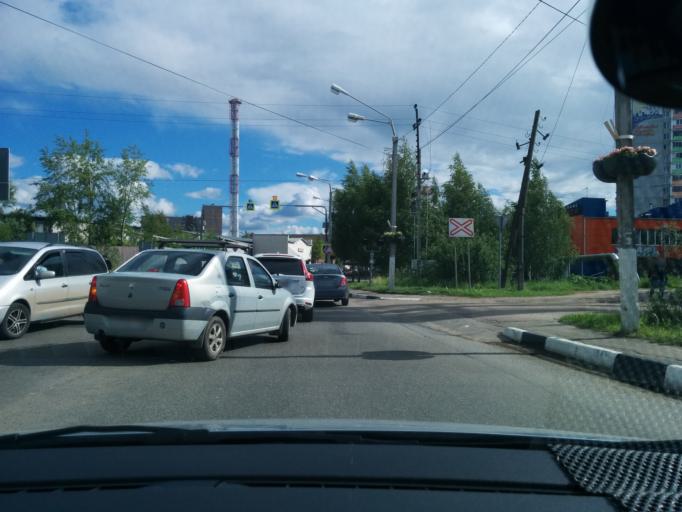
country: RU
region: Moskovskaya
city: Lobnya
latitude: 56.0196
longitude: 37.4723
